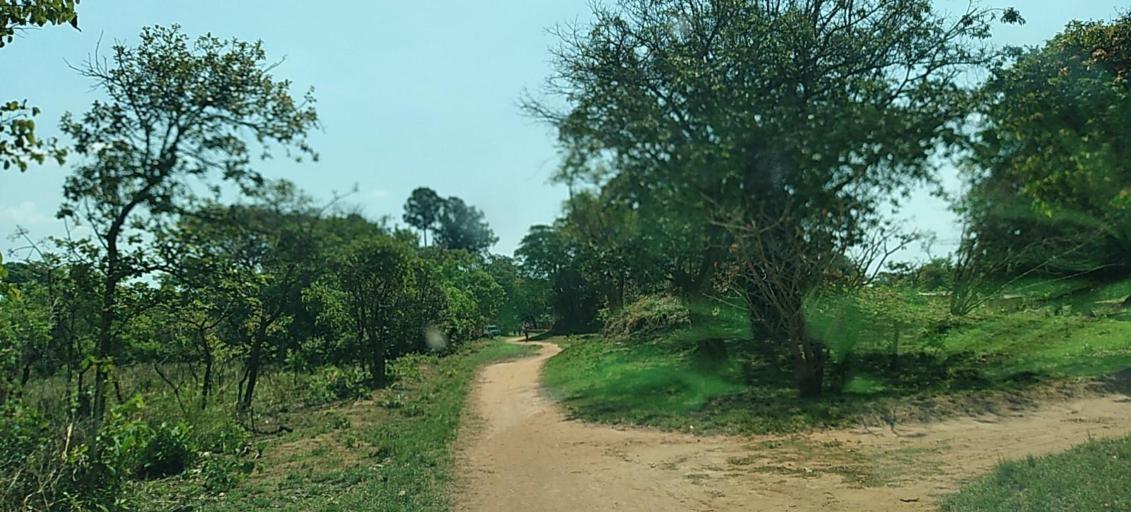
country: CD
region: Katanga
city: Kolwezi
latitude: -11.2791
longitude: 25.1283
